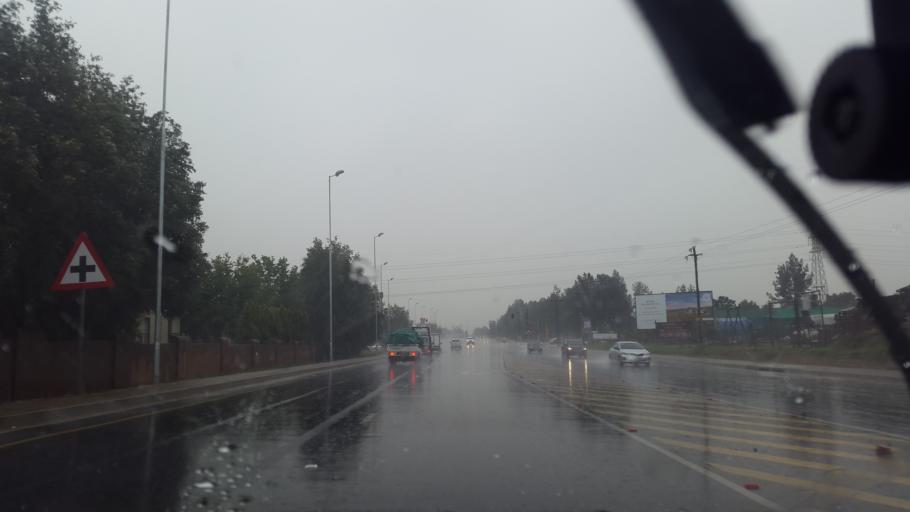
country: ZA
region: Gauteng
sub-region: City of Johannesburg Metropolitan Municipality
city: Diepsloot
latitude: -26.0042
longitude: 27.9879
